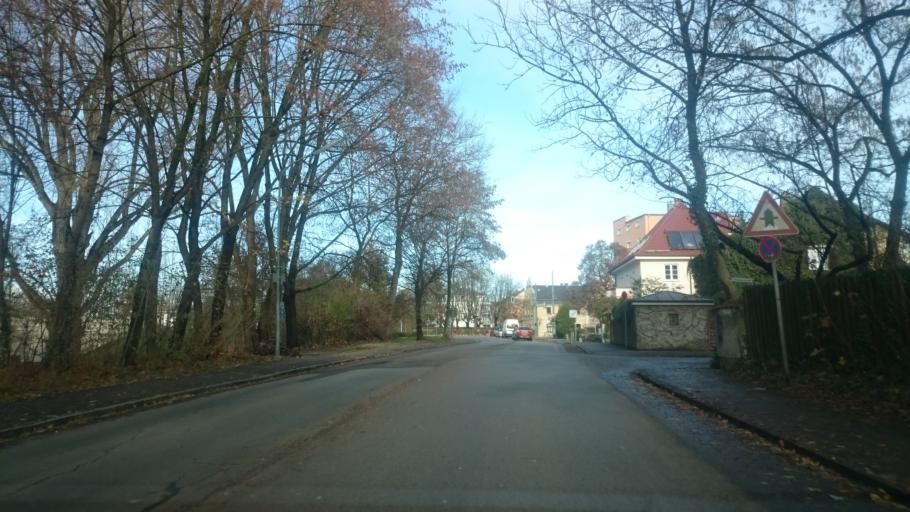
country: DE
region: Bavaria
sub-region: Swabia
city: Augsburg
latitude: 48.3540
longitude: 10.9382
